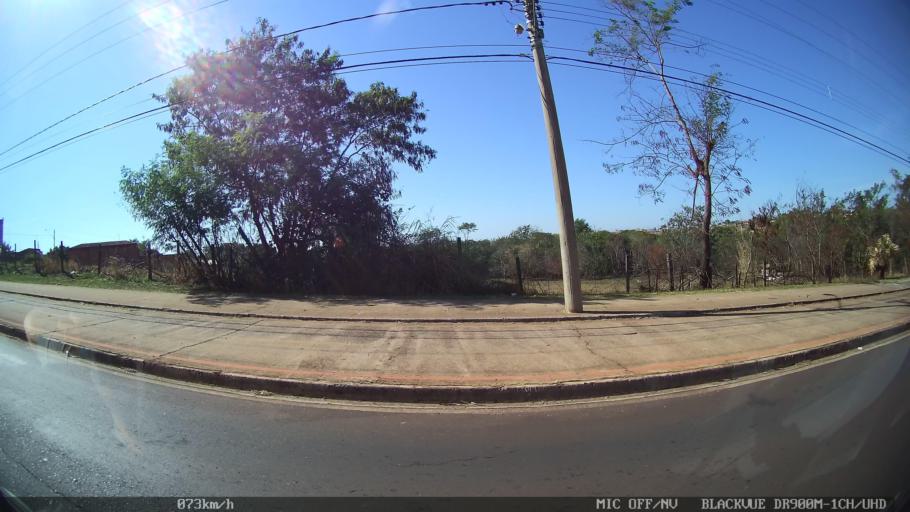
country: BR
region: Sao Paulo
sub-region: Batatais
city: Batatais
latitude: -20.9073
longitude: -47.5823
